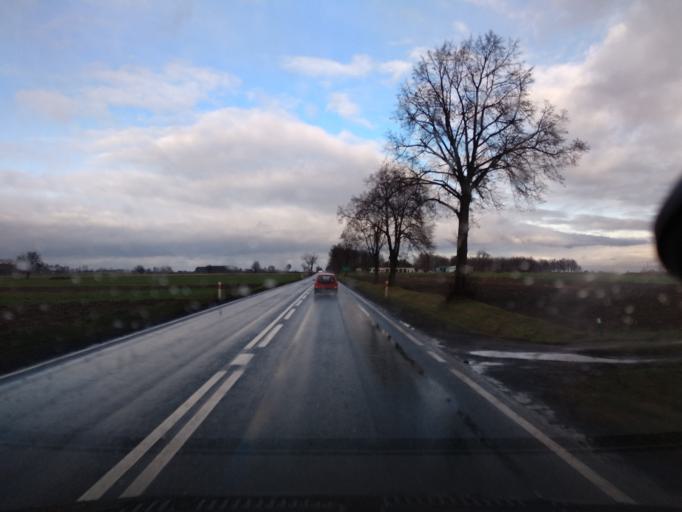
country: PL
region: Greater Poland Voivodeship
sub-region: Powiat koninski
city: Rychwal
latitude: 52.0417
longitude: 18.1619
